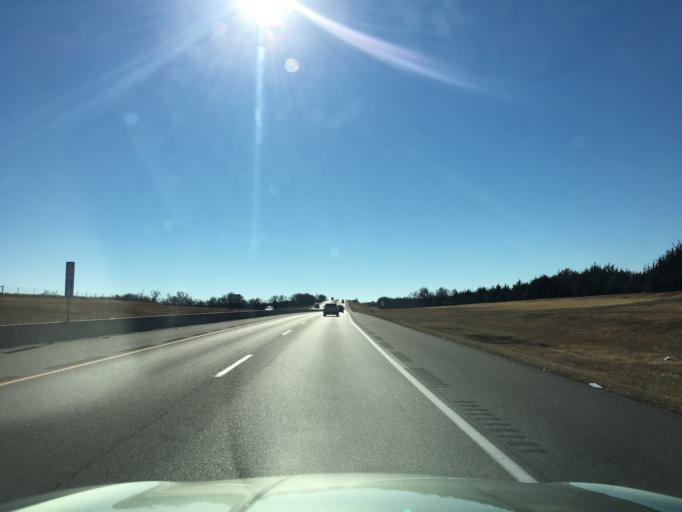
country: US
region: Kansas
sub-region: Sumner County
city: Belle Plaine
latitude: 37.3591
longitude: -97.3222
